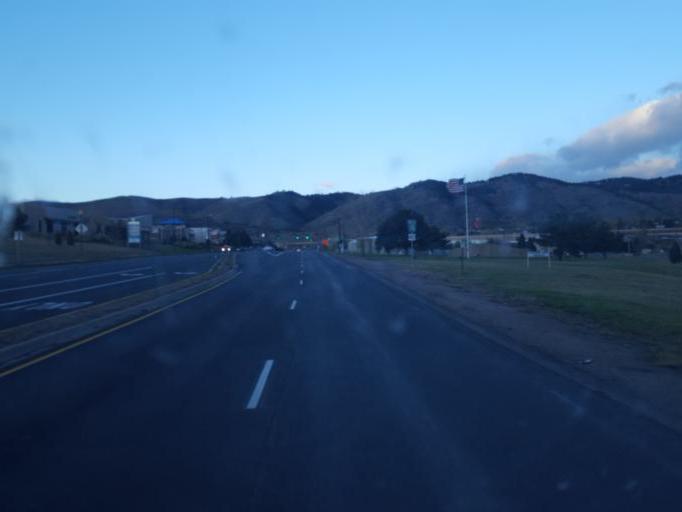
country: US
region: Colorado
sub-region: Jefferson County
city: West Pleasant View
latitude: 39.7251
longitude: -105.1896
